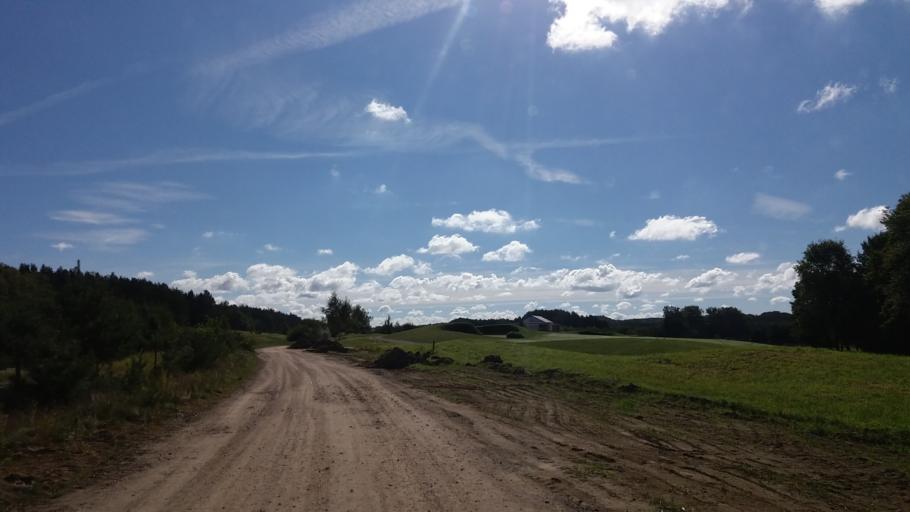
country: PL
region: West Pomeranian Voivodeship
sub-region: Powiat choszczenski
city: Krzecin
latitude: 53.1343
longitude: 15.4854
